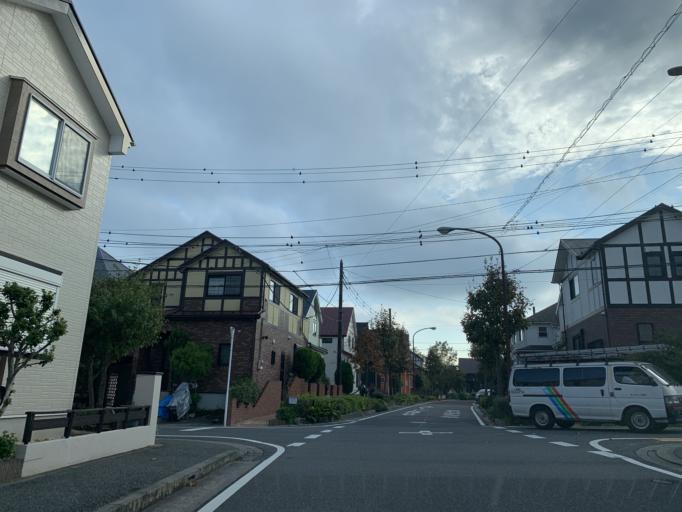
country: JP
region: Chiba
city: Nagareyama
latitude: 35.9125
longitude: 139.9142
